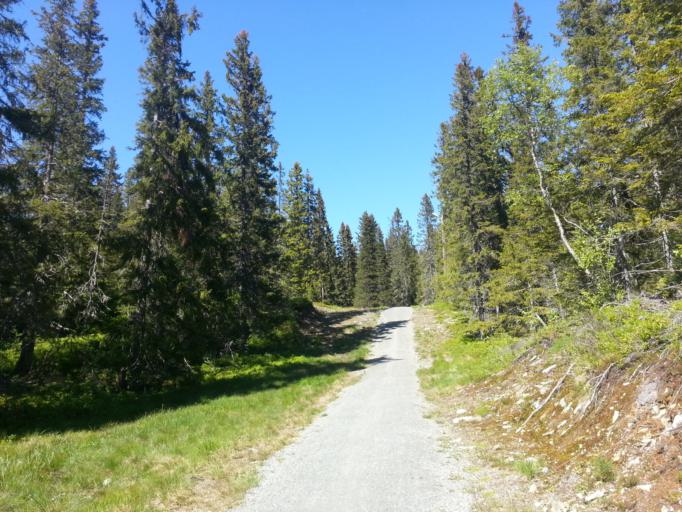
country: NO
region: Sor-Trondelag
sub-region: Trondheim
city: Trondheim
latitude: 63.4121
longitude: 10.2714
